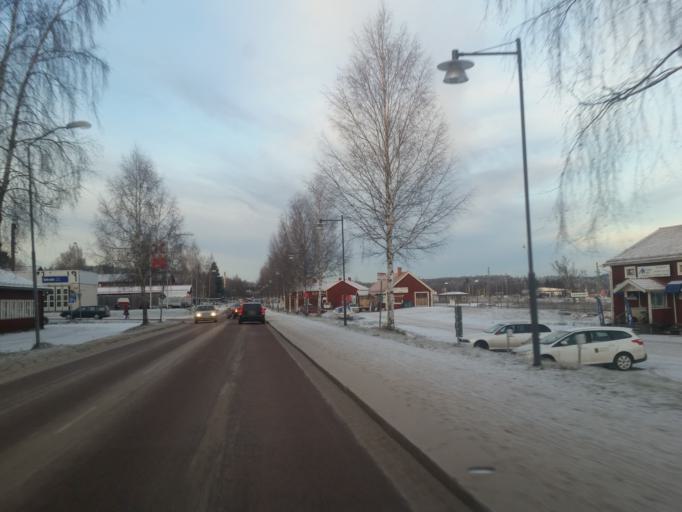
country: SE
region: Dalarna
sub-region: Leksand Municipality
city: Leksand
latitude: 60.7311
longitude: 15.0041
